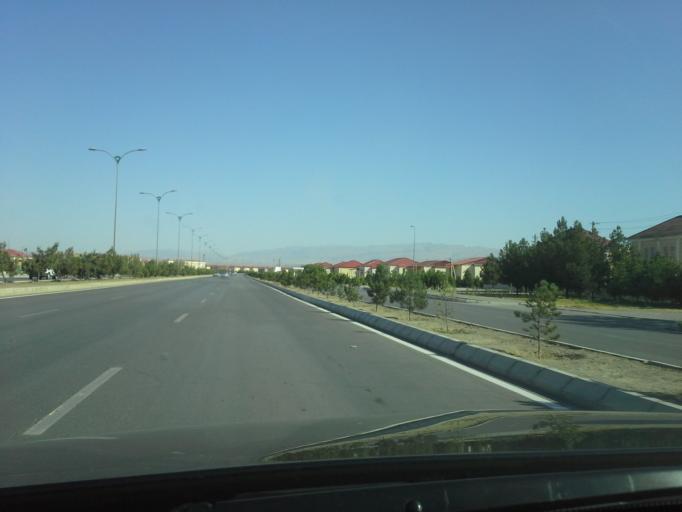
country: TM
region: Ahal
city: Ashgabat
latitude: 37.9987
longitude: 58.4072
